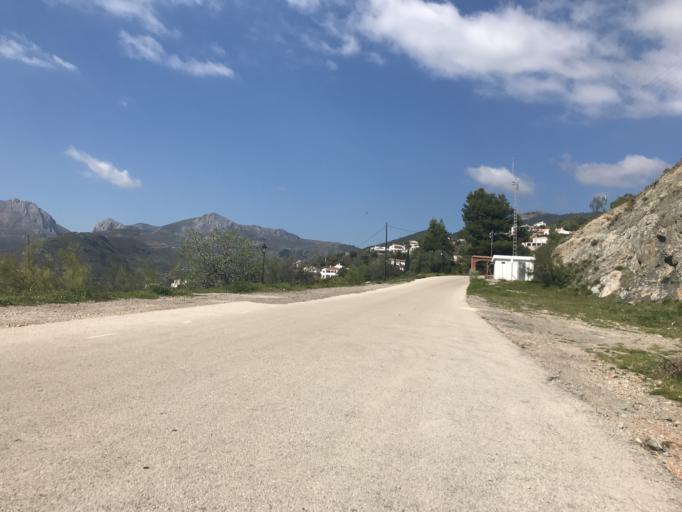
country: ES
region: Andalusia
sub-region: Provincia de Malaga
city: Alcaucin
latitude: 36.9053
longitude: -4.1125
